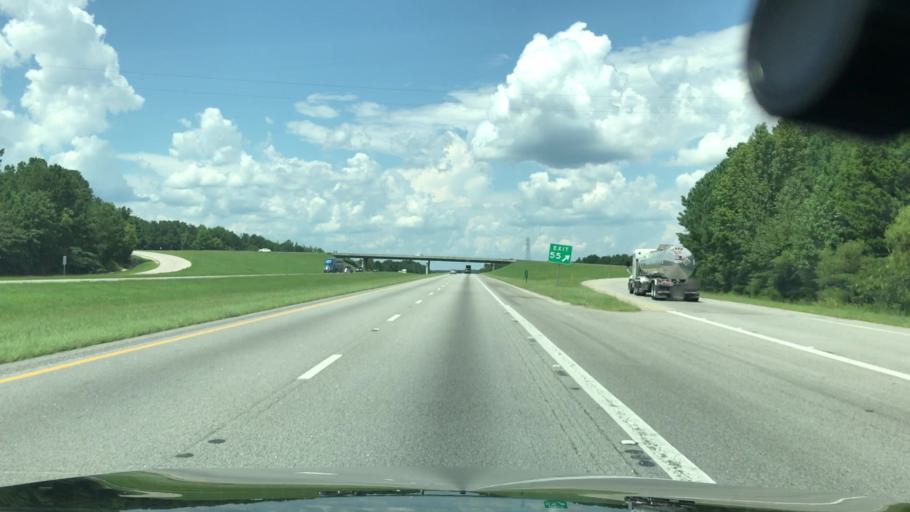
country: US
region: South Carolina
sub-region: Chester County
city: Great Falls
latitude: 34.6064
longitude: -81.0185
